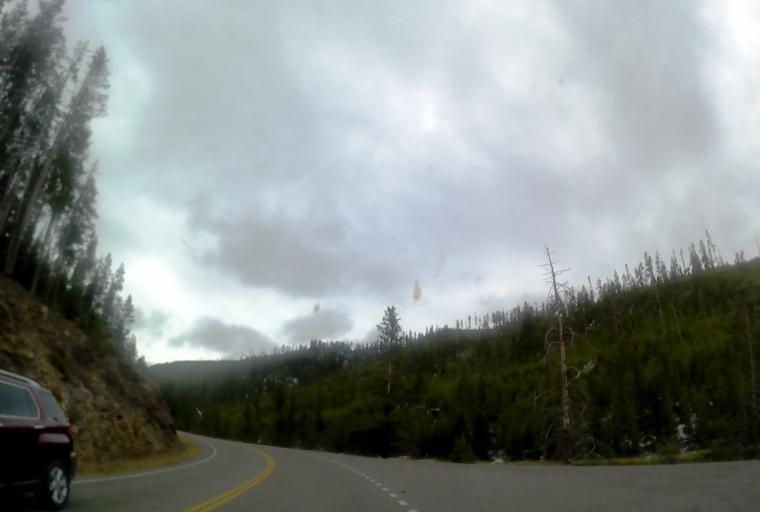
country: US
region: Montana
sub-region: Gallatin County
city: West Yellowstone
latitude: 44.6517
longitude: -111.0596
